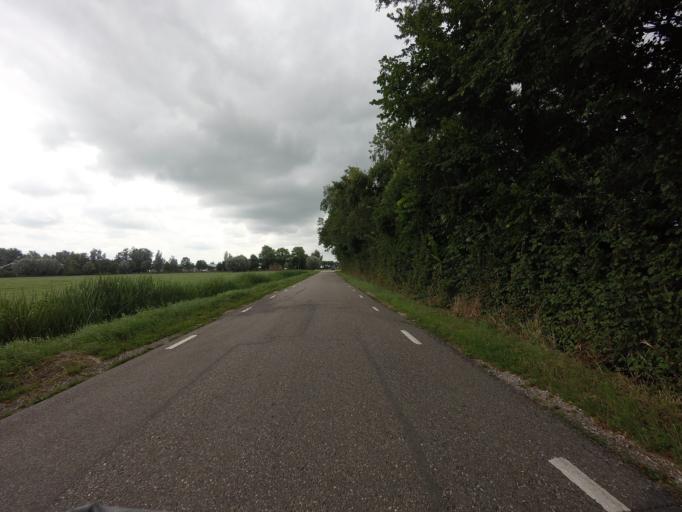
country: NL
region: South Holland
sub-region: Gemeente Giessenlanden
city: Giessenburg
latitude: 51.8930
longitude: 4.9036
